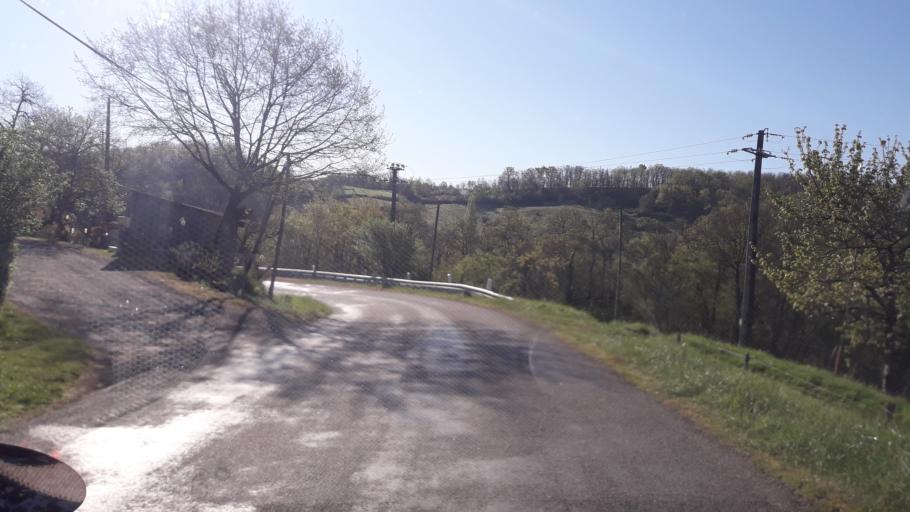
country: FR
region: Midi-Pyrenees
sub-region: Departement de la Haute-Garonne
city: Cazeres
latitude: 43.1938
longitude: 1.1419
